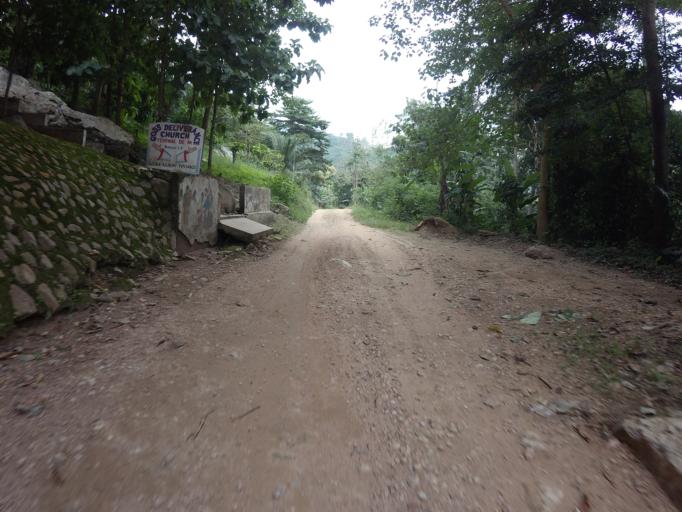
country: GH
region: Volta
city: Kpandu
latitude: 6.8785
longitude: 0.4413
